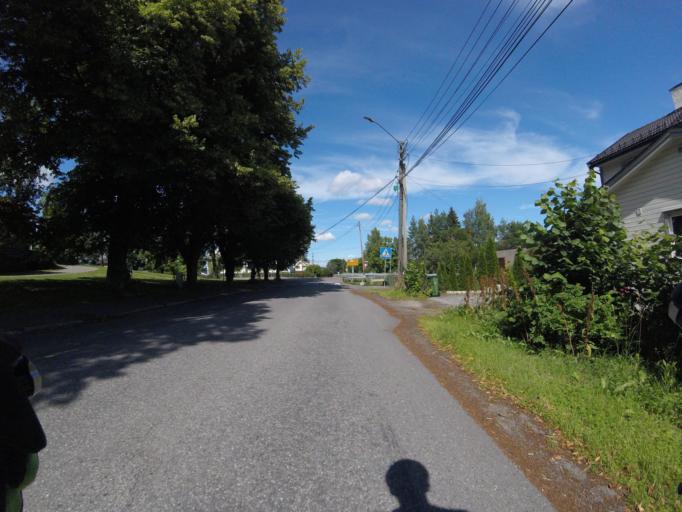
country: NO
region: Akershus
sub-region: Skedsmo
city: Lillestrom
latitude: 59.9526
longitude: 11.0158
